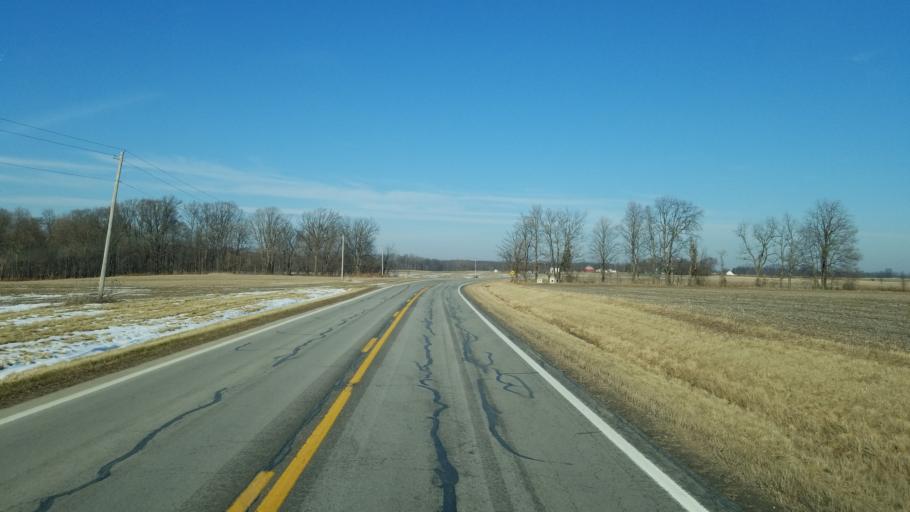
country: US
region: Ohio
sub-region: Huron County
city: Willard
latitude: 41.1242
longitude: -82.6616
